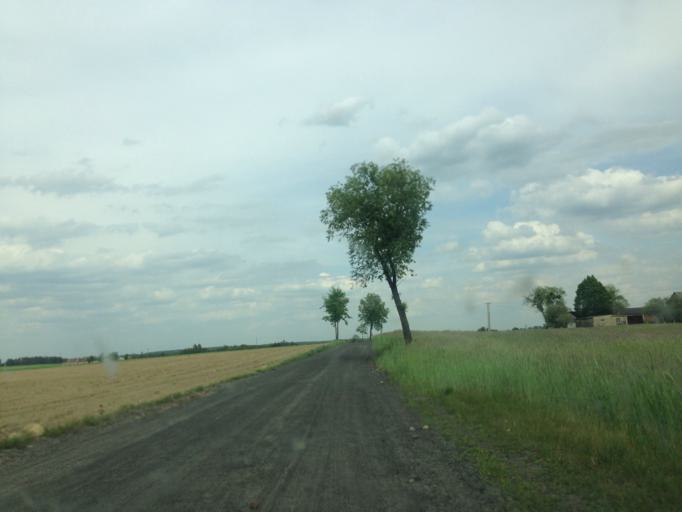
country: PL
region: Kujawsko-Pomorskie
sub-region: Powiat brodnicki
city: Brodnica
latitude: 53.3038
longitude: 19.3470
